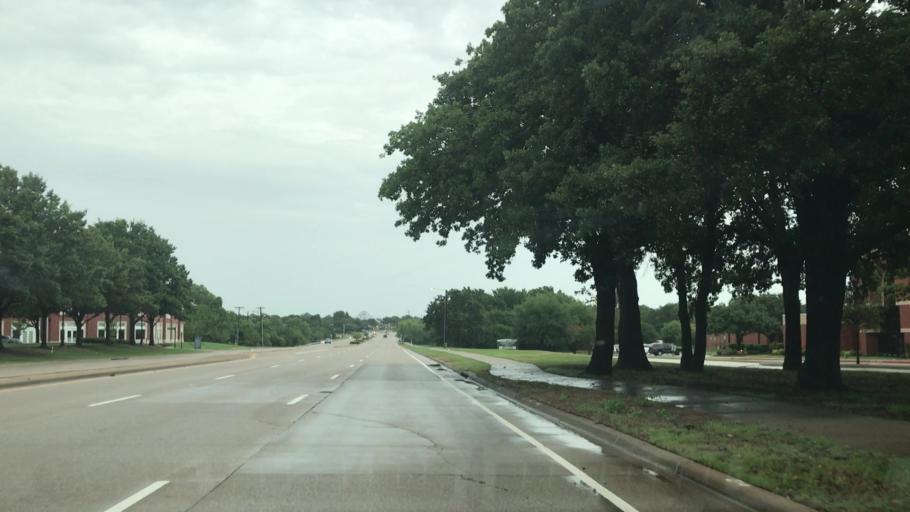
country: US
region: Texas
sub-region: Denton County
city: Flower Mound
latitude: 33.0381
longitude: -97.0505
